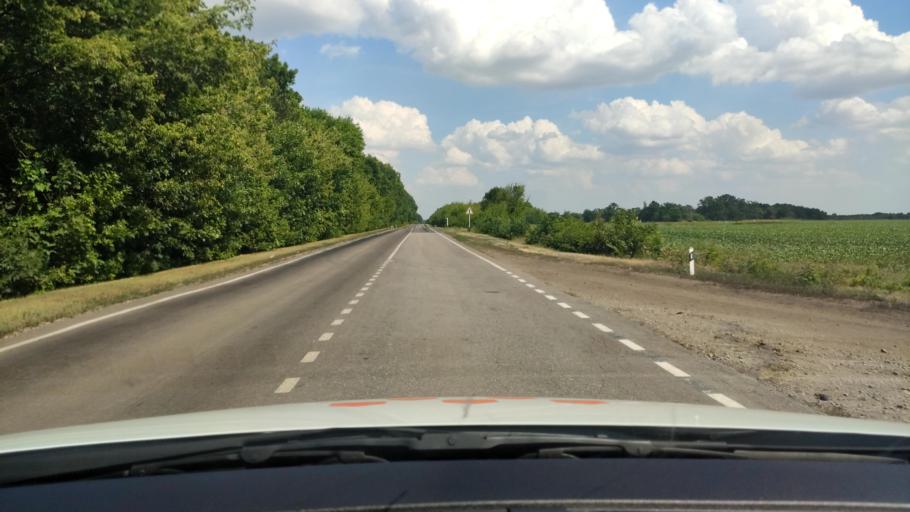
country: RU
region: Voronezj
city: Ertil'
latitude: 51.7890
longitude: 40.6463
